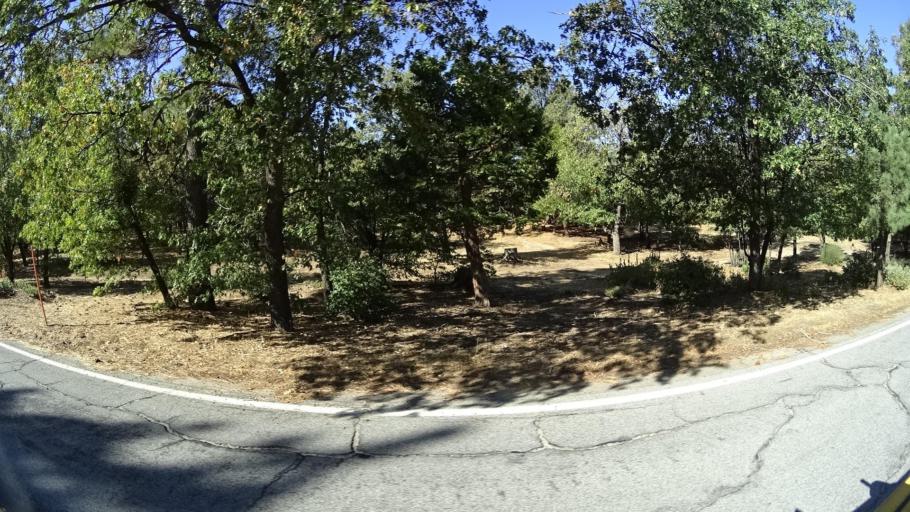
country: US
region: California
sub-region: San Diego County
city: Pine Valley
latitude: 32.8713
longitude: -116.4160
